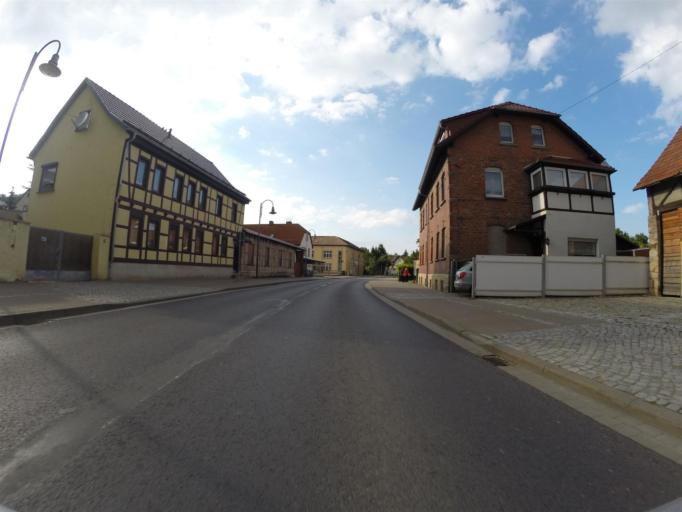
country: DE
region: Thuringia
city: Kranichfeld
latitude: 50.8550
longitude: 11.2022
